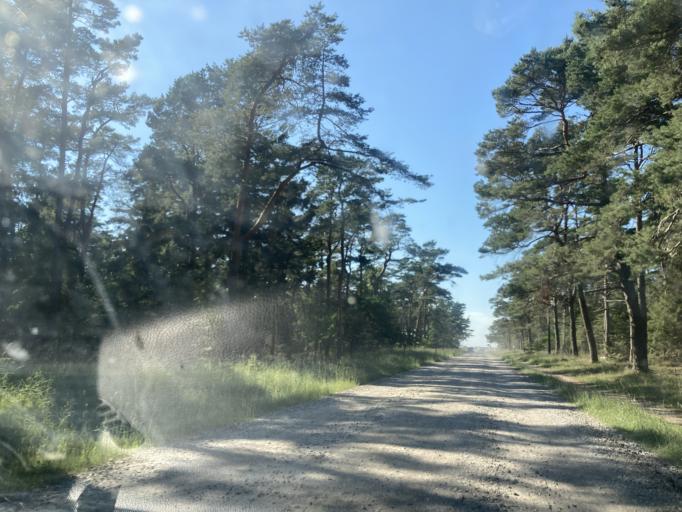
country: DK
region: Capital Region
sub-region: Halsnaes Kommune
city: Frederiksvaerk
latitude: 56.0203
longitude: 12.0058
